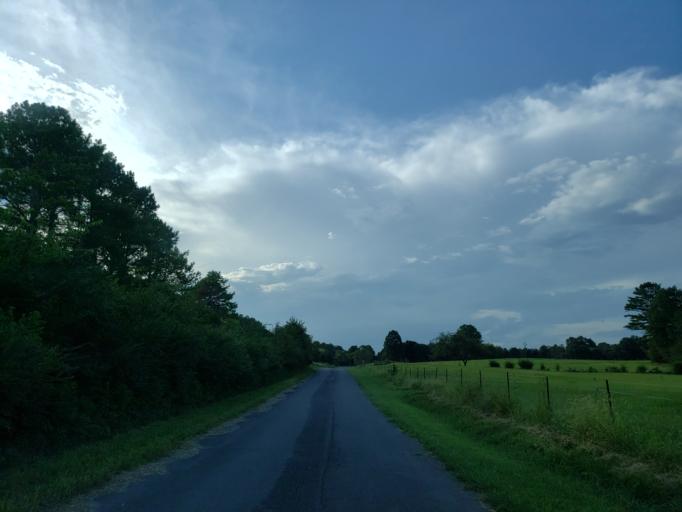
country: US
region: Georgia
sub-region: Bartow County
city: Euharlee
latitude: 34.2406
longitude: -84.9528
